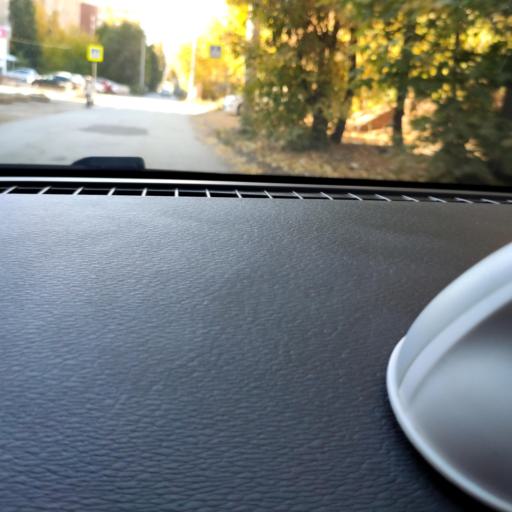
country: RU
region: Samara
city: Samara
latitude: 53.1948
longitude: 50.1444
